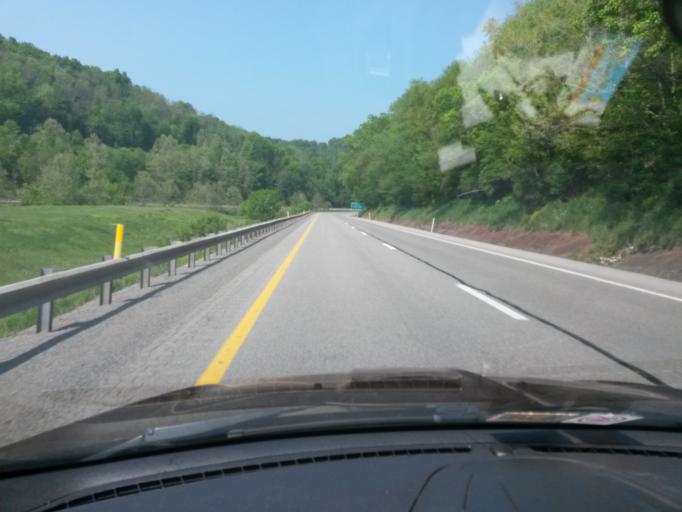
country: US
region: West Virginia
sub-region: Lewis County
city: Weston
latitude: 38.9995
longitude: -80.3777
